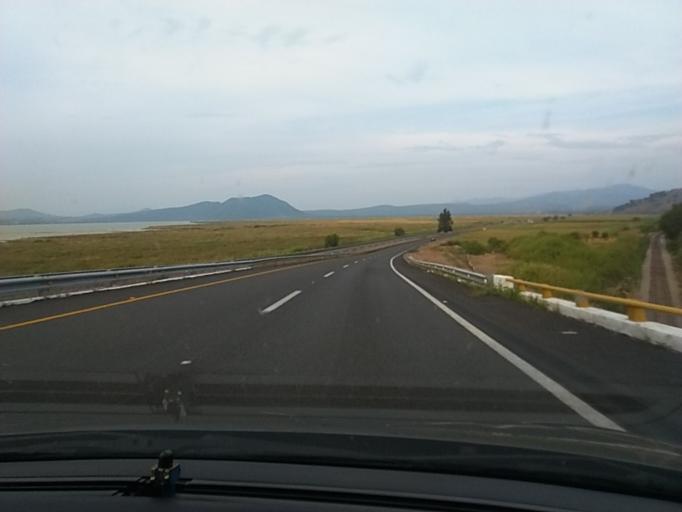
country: MX
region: Michoacan
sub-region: Zinapecuaro
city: Jose Maria Morelos (La Yegueeria)
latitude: 19.8966
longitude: -100.8971
